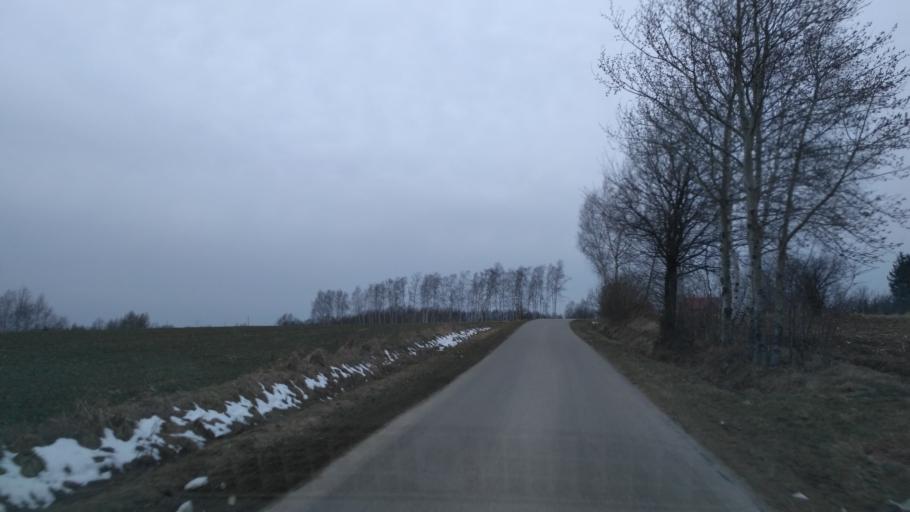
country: PL
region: Subcarpathian Voivodeship
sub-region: Powiat rzeszowski
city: Chmielnik
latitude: 49.9884
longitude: 22.1490
